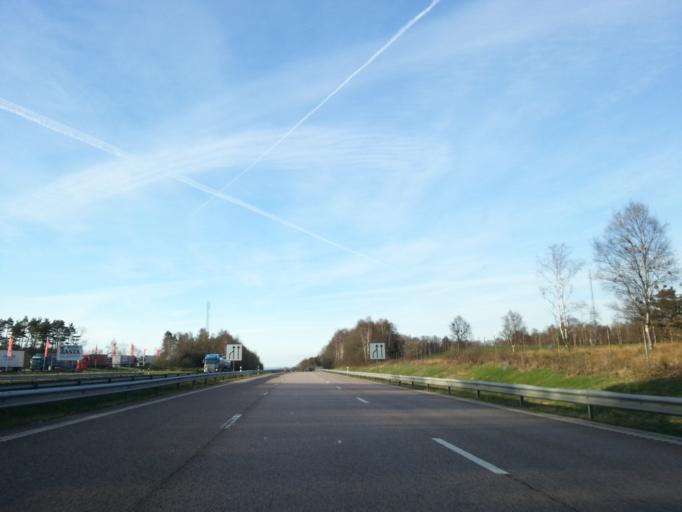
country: SE
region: Skane
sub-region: Bastads Kommun
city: Bastad
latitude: 56.3875
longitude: 12.9381
